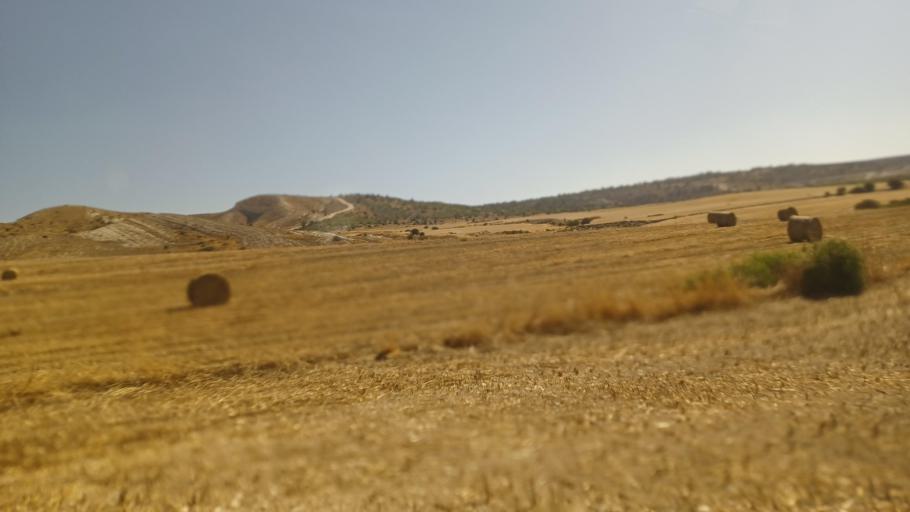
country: CY
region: Larnaka
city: Voroklini
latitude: 35.0092
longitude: 33.6483
